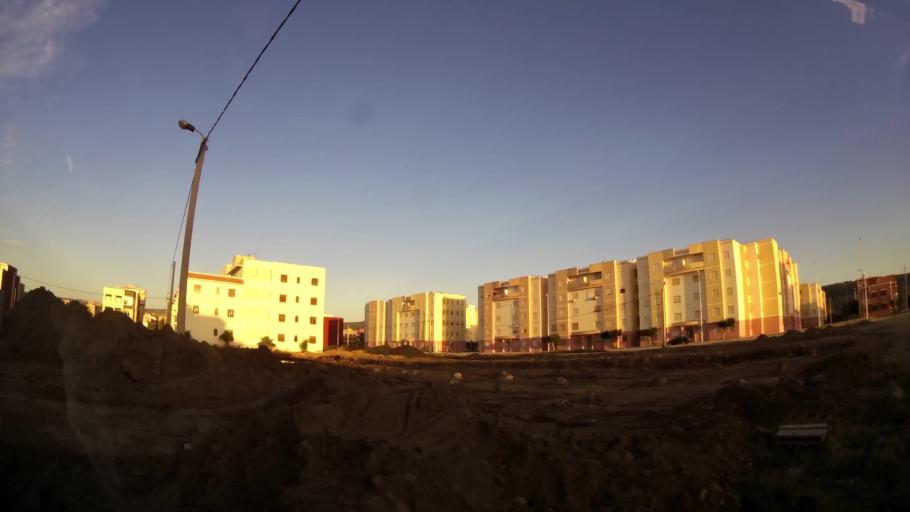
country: MA
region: Oriental
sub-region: Berkane-Taourirt
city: Madagh
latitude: 35.0782
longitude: -2.2333
